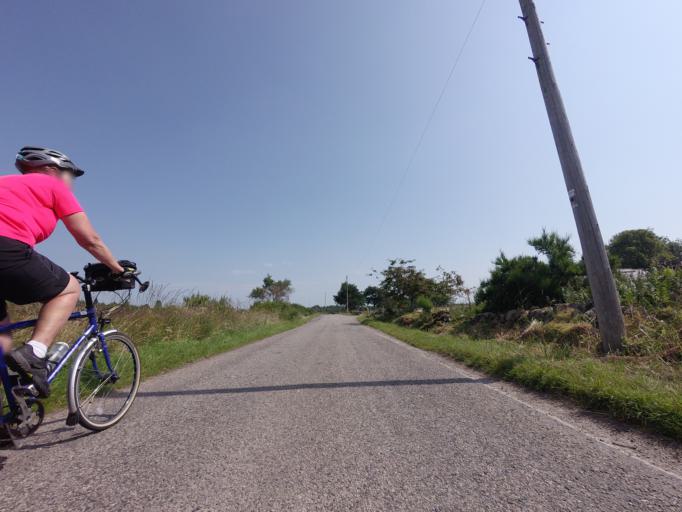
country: GB
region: Scotland
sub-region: Highland
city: Tain
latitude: 57.7931
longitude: -4.0802
